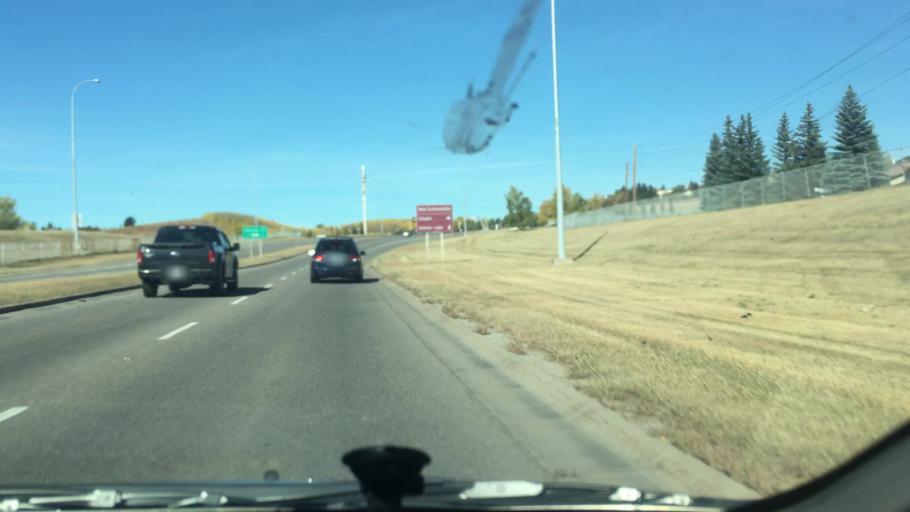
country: CA
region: Alberta
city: Calgary
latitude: 51.1187
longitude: -114.1628
